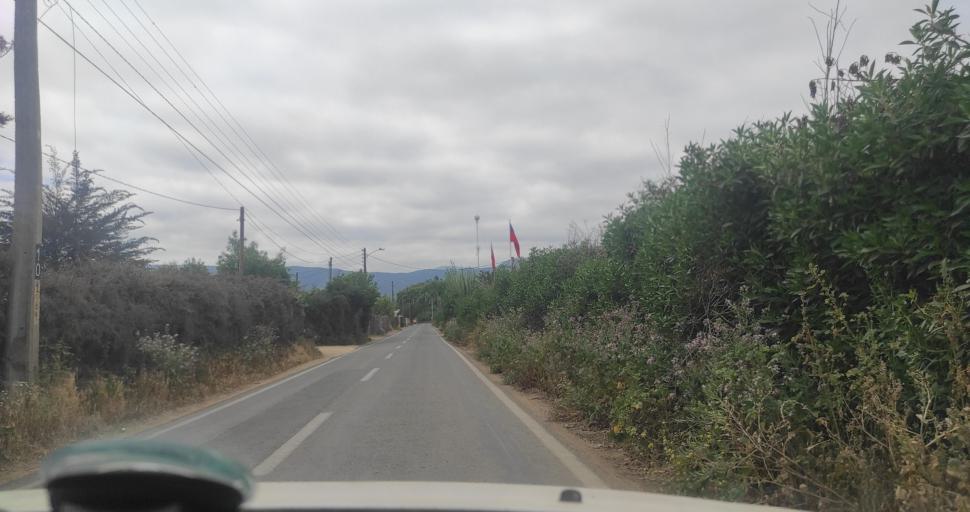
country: CL
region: Valparaiso
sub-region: Provincia de Marga Marga
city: Limache
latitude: -33.0321
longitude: -71.2406
